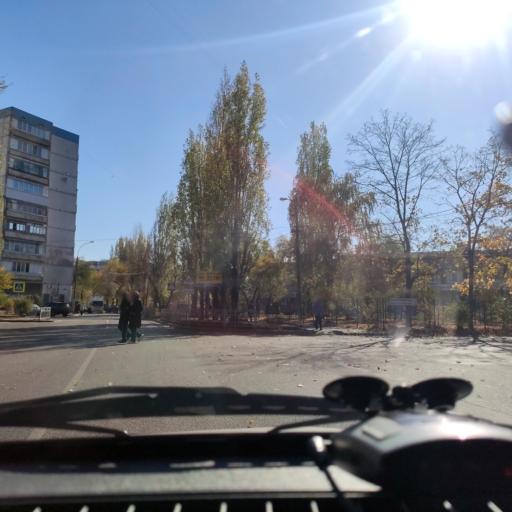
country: RU
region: Voronezj
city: Voronezh
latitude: 51.6501
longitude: 39.1436
